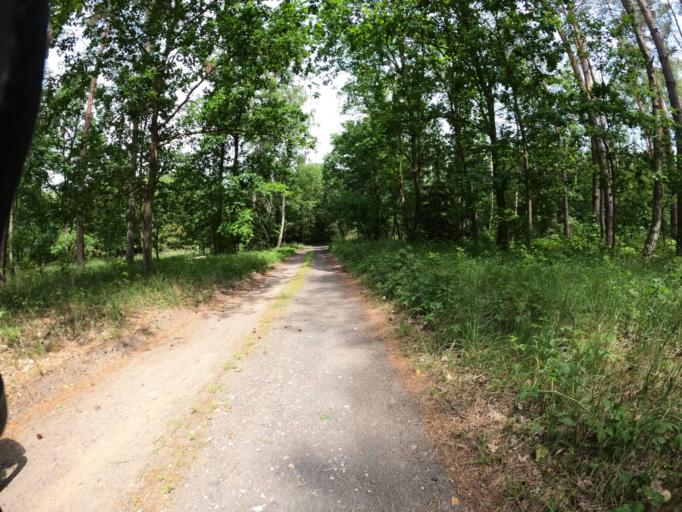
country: PL
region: West Pomeranian Voivodeship
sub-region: Powiat mysliborski
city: Boleszkowice
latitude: 52.6883
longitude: 14.4943
